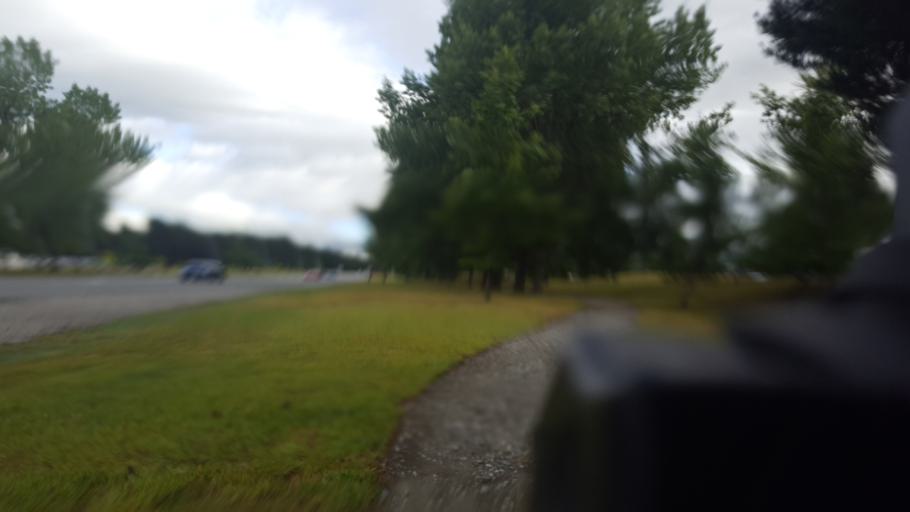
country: NZ
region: Otago
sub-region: Queenstown-Lakes District
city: Wanaka
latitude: -45.2430
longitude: 169.3780
